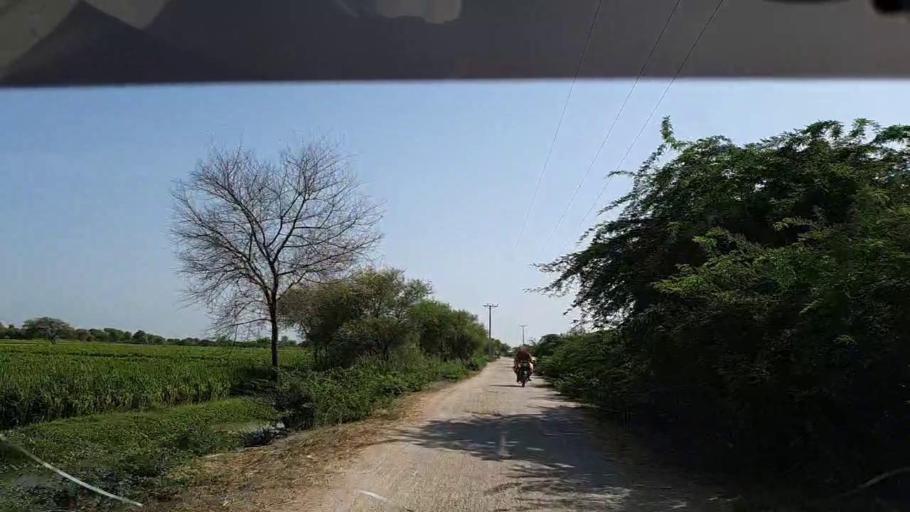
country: PK
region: Sindh
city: Badin
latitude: 24.6464
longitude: 68.7879
